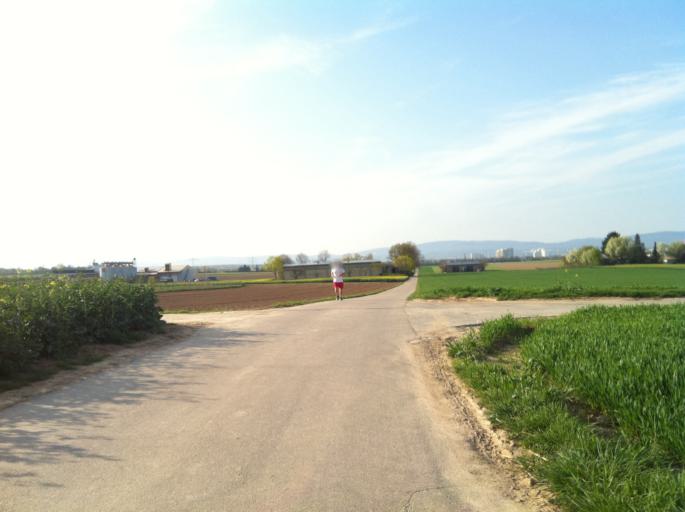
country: DE
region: Rheinland-Pfalz
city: Klein-Winternheim
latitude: 49.9738
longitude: 8.2240
